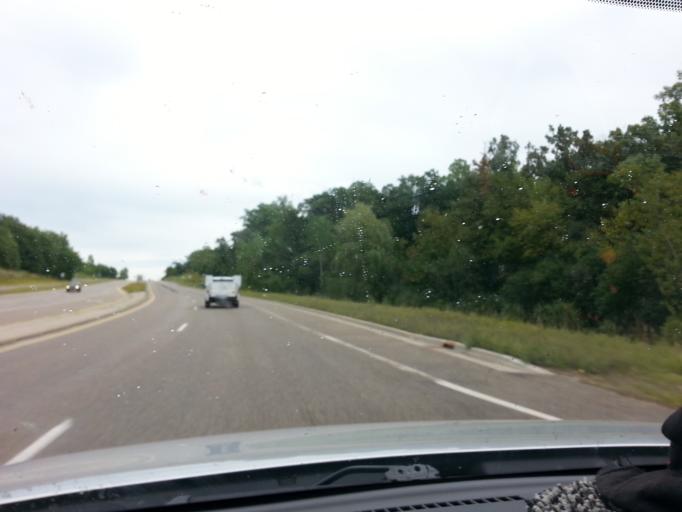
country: US
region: Minnesota
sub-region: Scott County
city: Prior Lake
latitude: 44.6814
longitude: -93.3505
